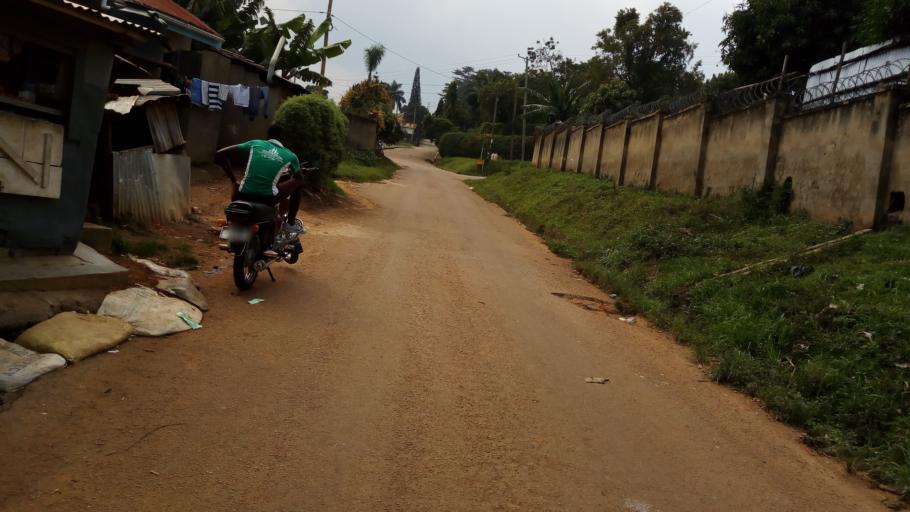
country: UG
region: Central Region
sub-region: Wakiso District
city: Kireka
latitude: 0.3114
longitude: 32.6415
